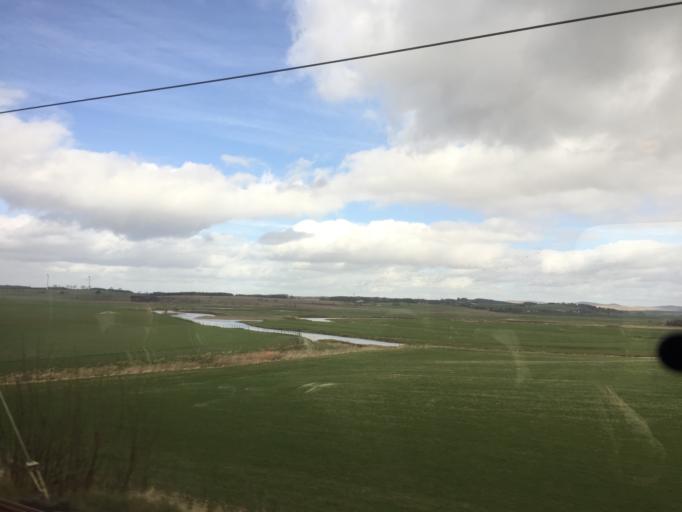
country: GB
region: Scotland
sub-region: South Lanarkshire
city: Carnwath
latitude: 55.6723
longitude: -3.6422
